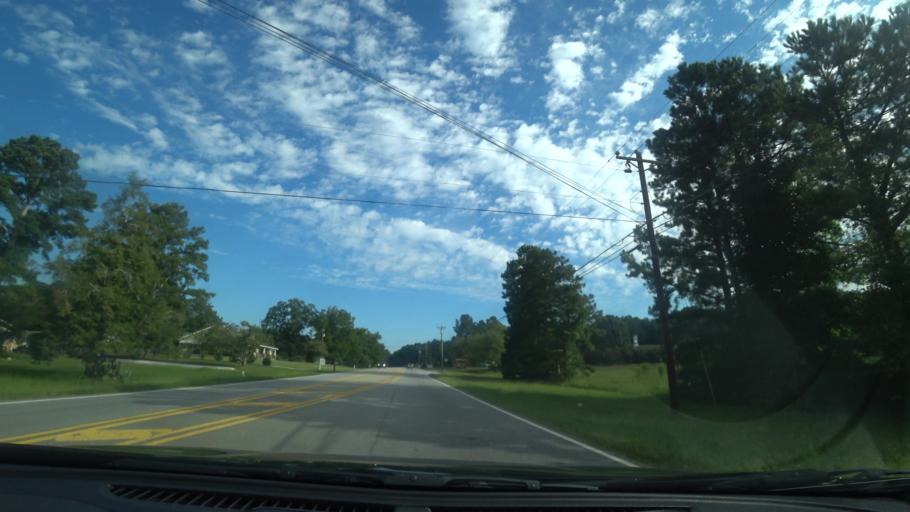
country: US
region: Georgia
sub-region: Rockdale County
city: Lakeview Estates
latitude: 33.7089
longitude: -84.0038
